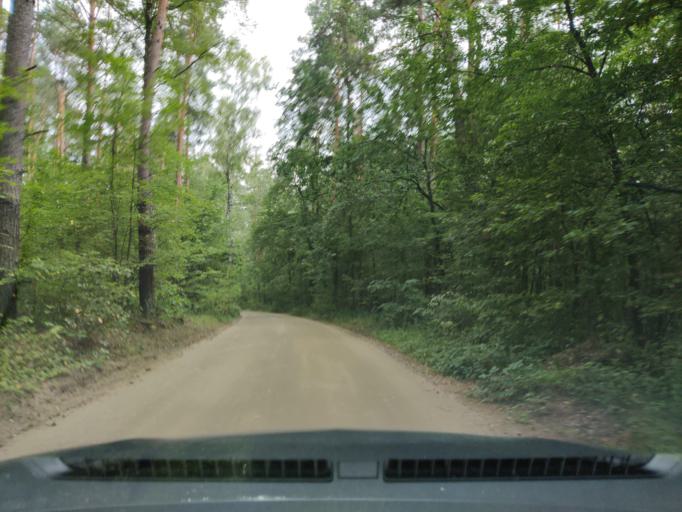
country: PL
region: Masovian Voivodeship
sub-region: Powiat pultuski
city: Pultusk
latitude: 52.7580
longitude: 21.1411
